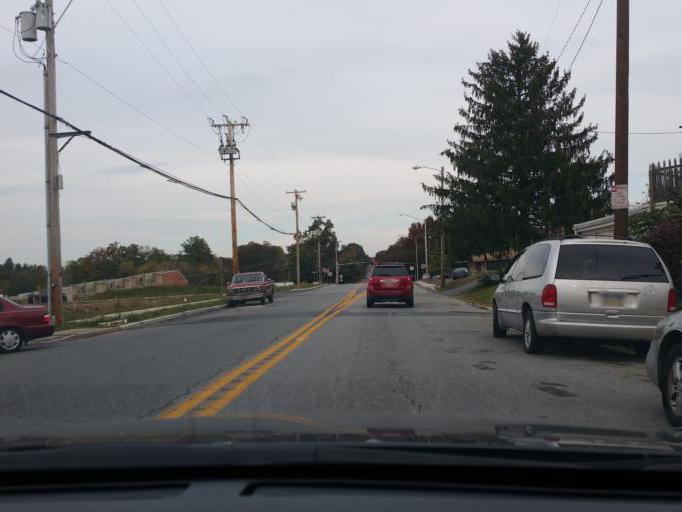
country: US
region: Pennsylvania
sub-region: Lancaster County
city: Lancaster
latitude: 40.0288
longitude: -76.2930
